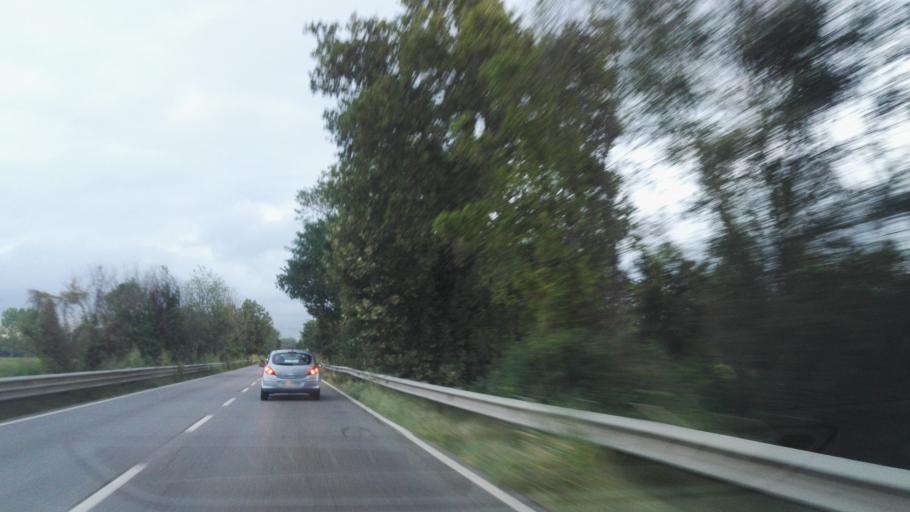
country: IT
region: Lombardy
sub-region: Citta metropolitana di Milano
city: Settala
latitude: 45.4602
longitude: 9.4026
